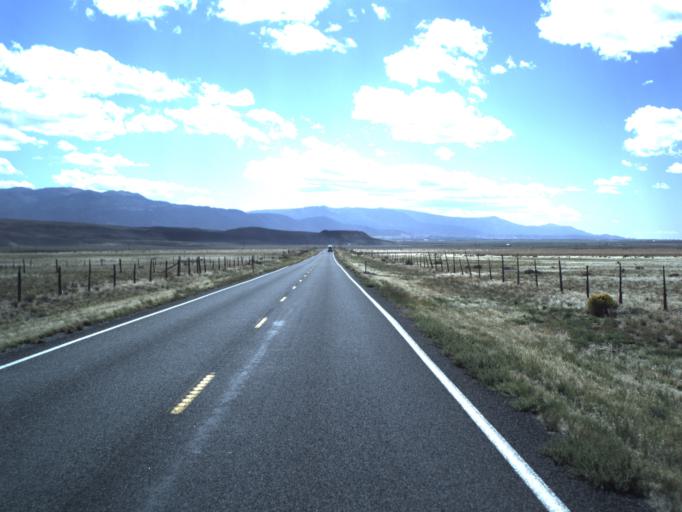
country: US
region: Utah
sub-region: Iron County
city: Enoch
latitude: 37.8985
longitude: -113.0316
